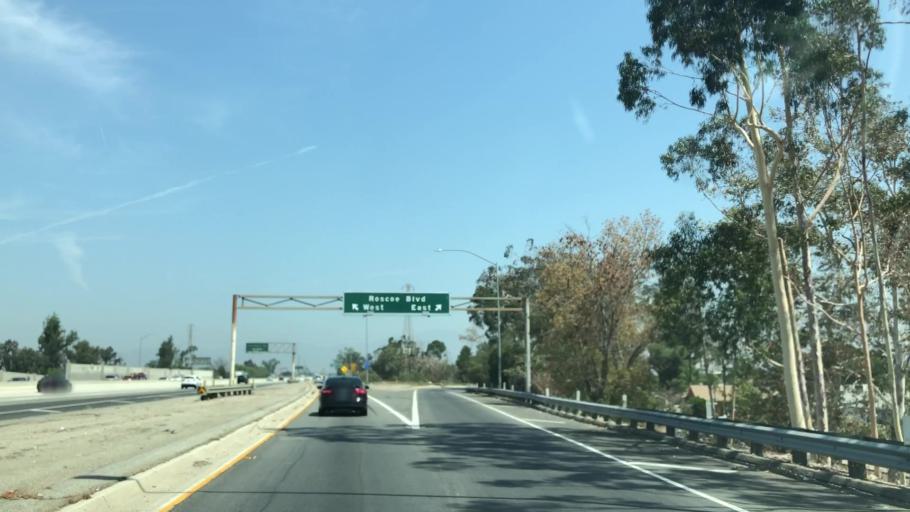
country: US
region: California
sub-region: Los Angeles County
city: Van Nuys
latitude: 34.2189
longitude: -118.4091
